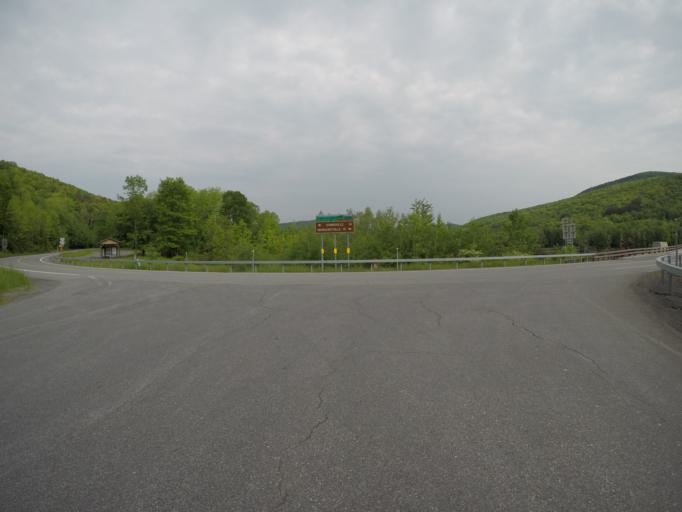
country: US
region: New York
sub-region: Sullivan County
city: Livingston Manor
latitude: 42.0862
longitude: -74.8207
